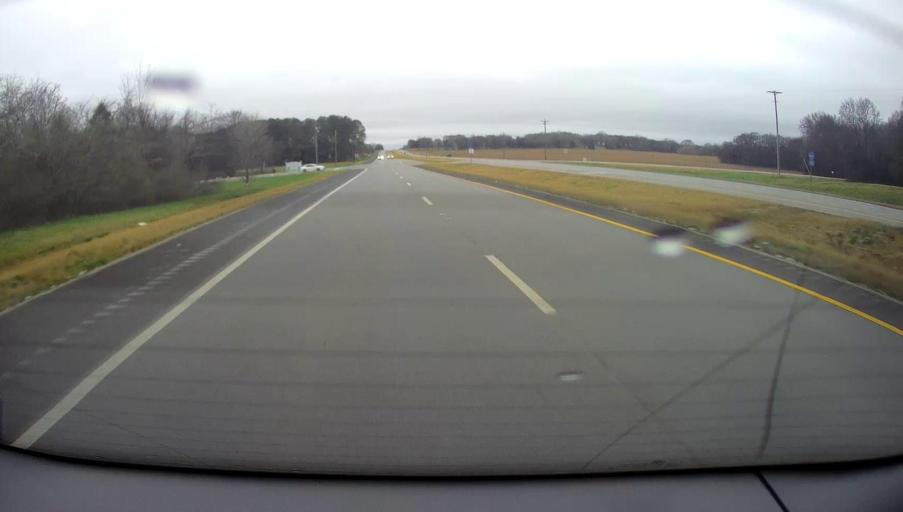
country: US
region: Alabama
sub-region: Lawrence County
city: Town Creek
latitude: 34.6797
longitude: -87.3514
